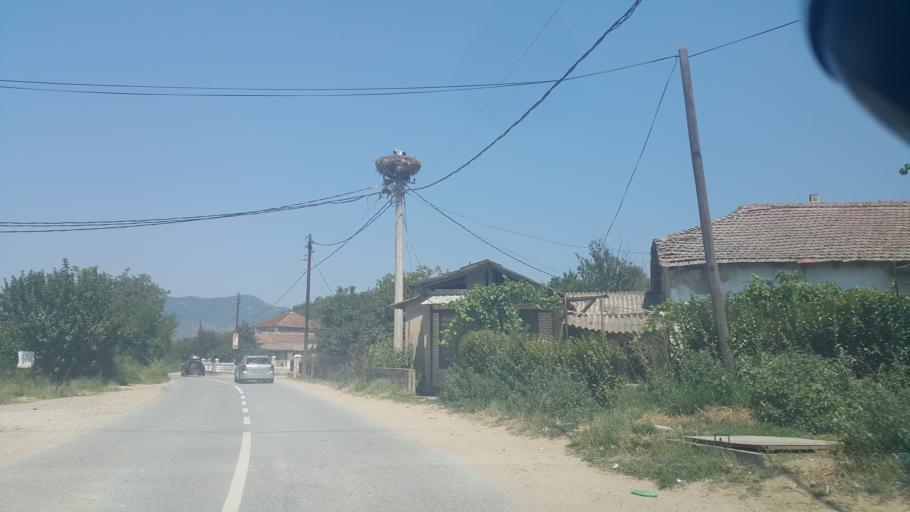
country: MK
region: Valandovo
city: Pirava
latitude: 41.2836
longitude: 22.4981
